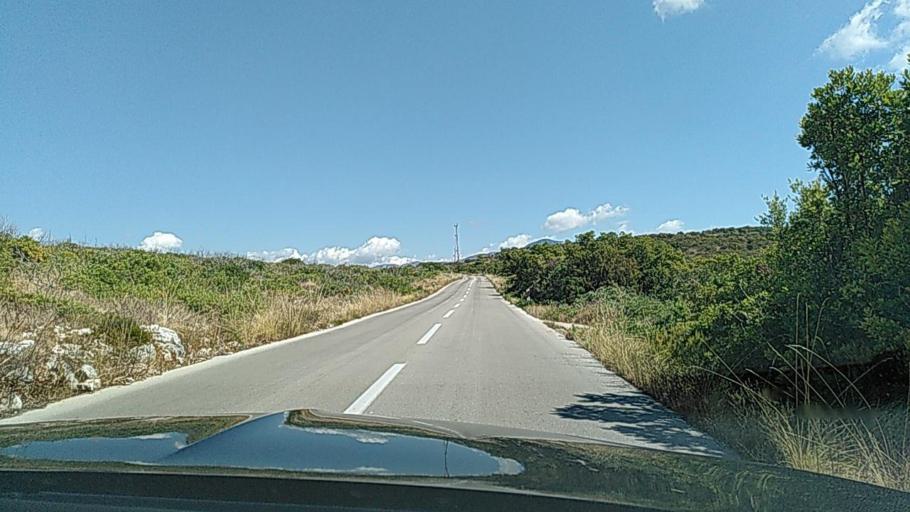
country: HR
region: Dubrovacko-Neretvanska
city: Orebic
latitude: 43.1249
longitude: 17.1221
